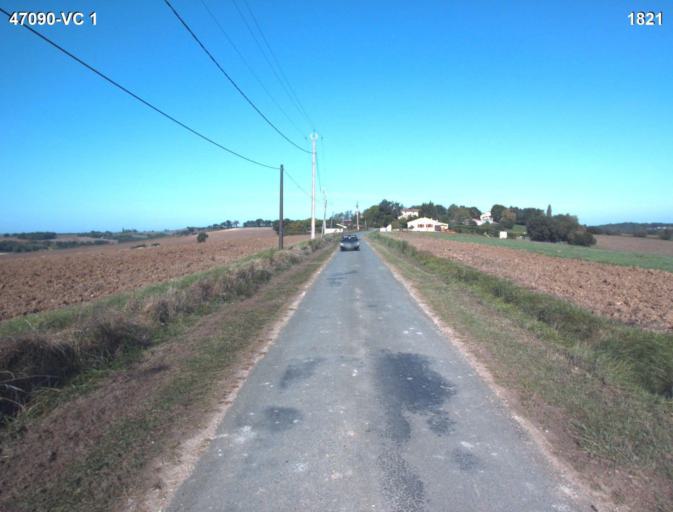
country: FR
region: Aquitaine
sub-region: Departement du Lot-et-Garonne
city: Nerac
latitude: 44.1603
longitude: 0.3881
